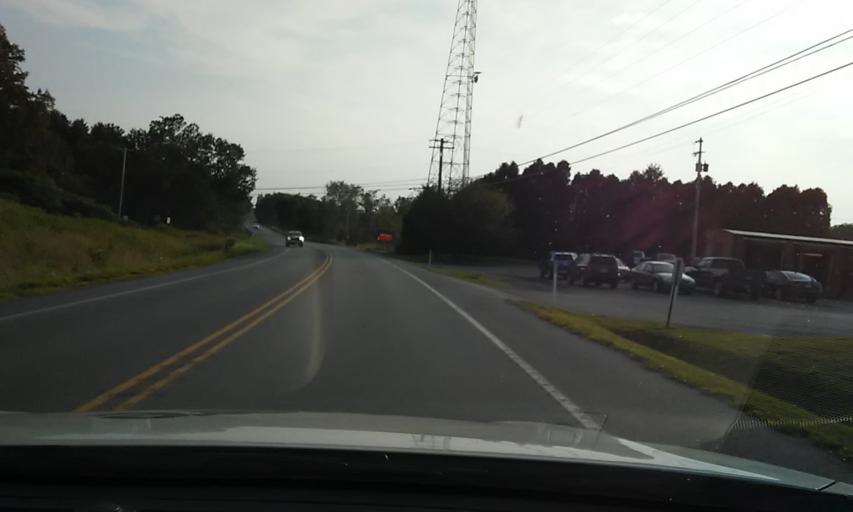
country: US
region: Pennsylvania
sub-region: McKean County
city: Kane
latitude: 41.6726
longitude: -78.7658
